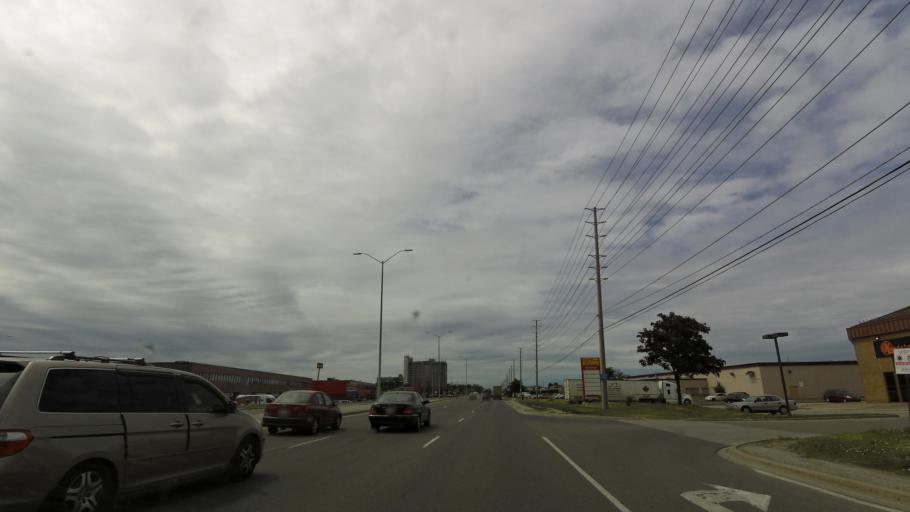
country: CA
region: Ontario
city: Etobicoke
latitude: 43.6392
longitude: -79.6252
